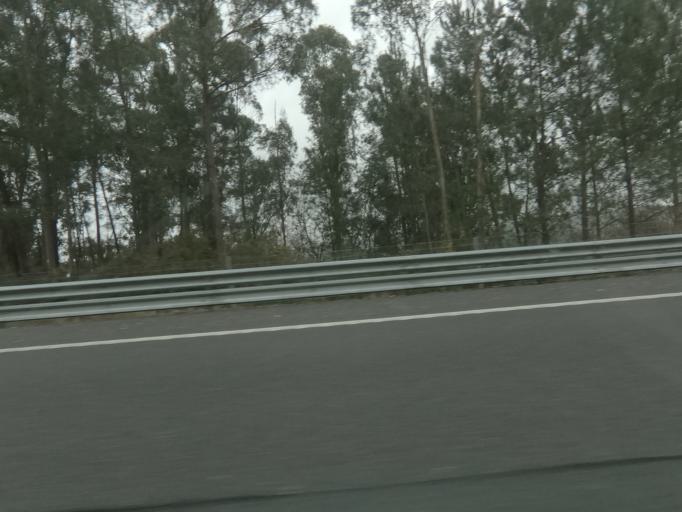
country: ES
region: Galicia
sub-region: Provincia da Coruna
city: Santiago de Compostela
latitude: 42.8439
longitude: -8.5308
